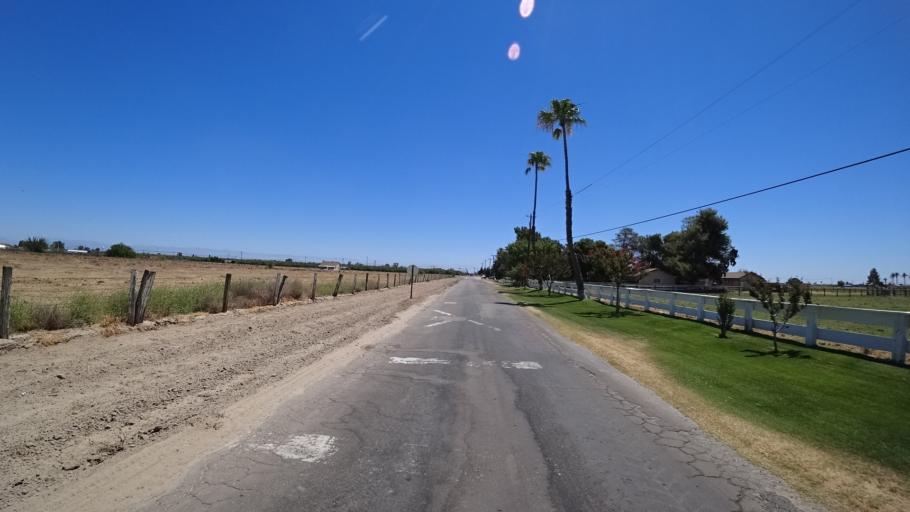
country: US
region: California
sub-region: Fresno County
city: Easton
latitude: 36.6707
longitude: -119.7489
